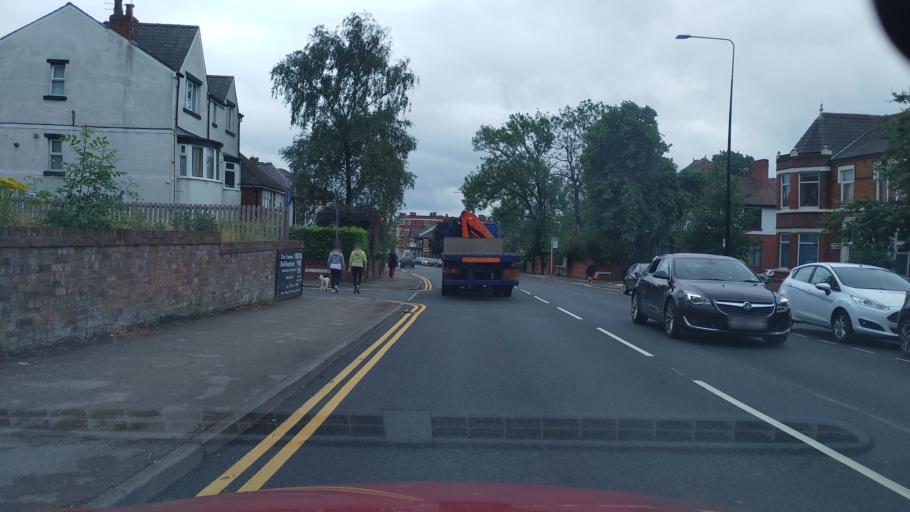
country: GB
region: England
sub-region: Borough of Wigan
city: Ince-in-Makerfield
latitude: 53.5568
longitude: -2.6284
